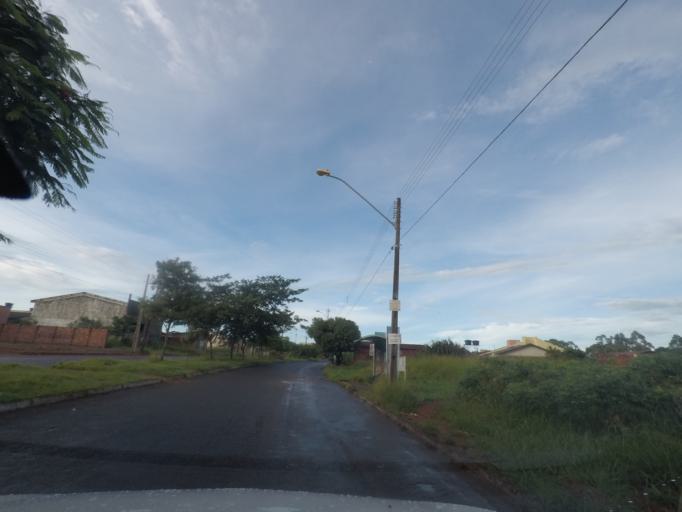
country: BR
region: Goias
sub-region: Goiania
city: Goiania
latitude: -16.7463
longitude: -49.3735
